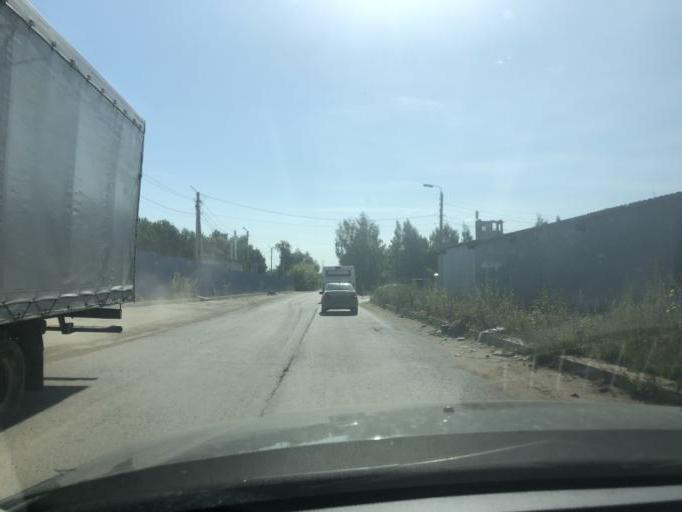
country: RU
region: Tula
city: Skuratovskiy
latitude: 54.1277
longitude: 37.6259
